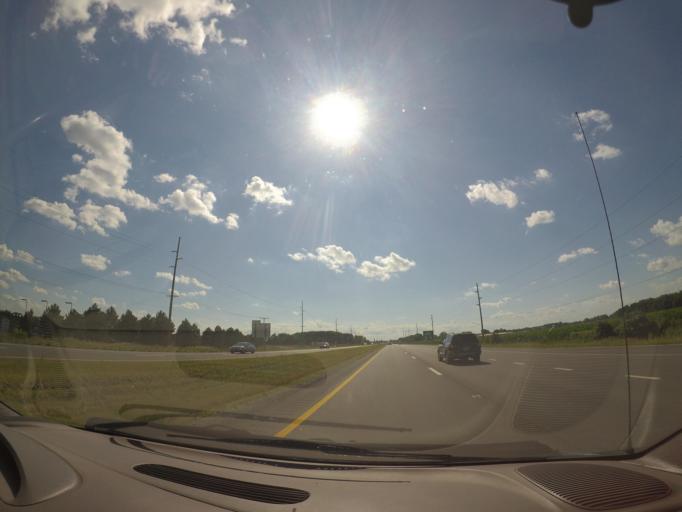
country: US
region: Ohio
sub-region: Sandusky County
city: Fremont
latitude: 41.3678
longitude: -83.1216
